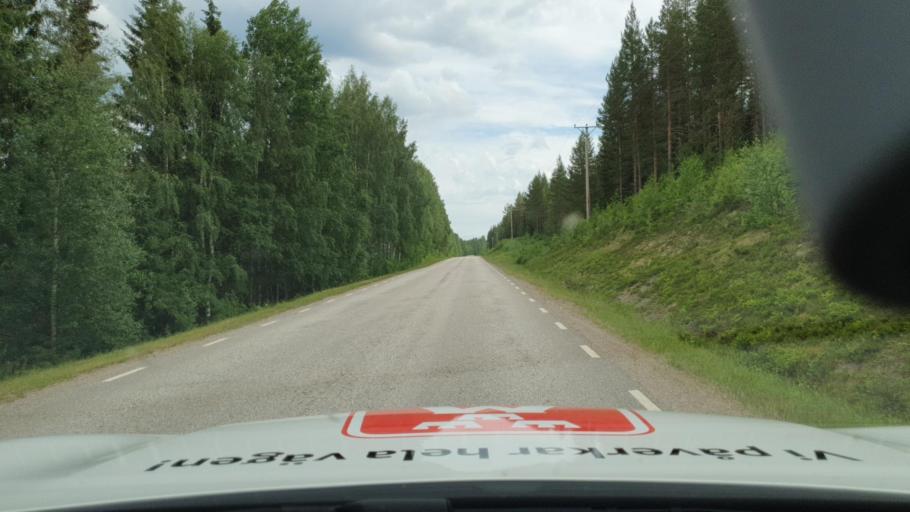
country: NO
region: Hedmark
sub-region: Trysil
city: Innbygda
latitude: 61.0152
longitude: 12.4752
